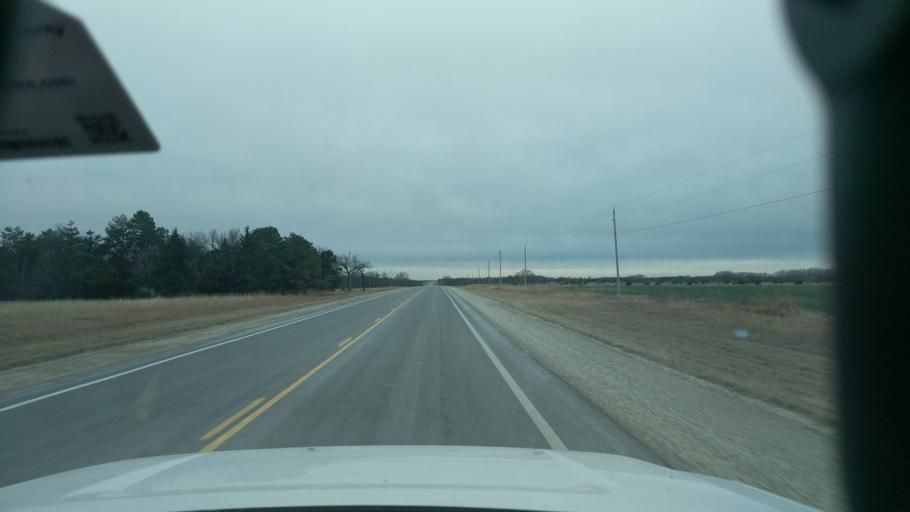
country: US
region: Kansas
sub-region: Marion County
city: Marion
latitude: 38.4808
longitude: -96.9577
